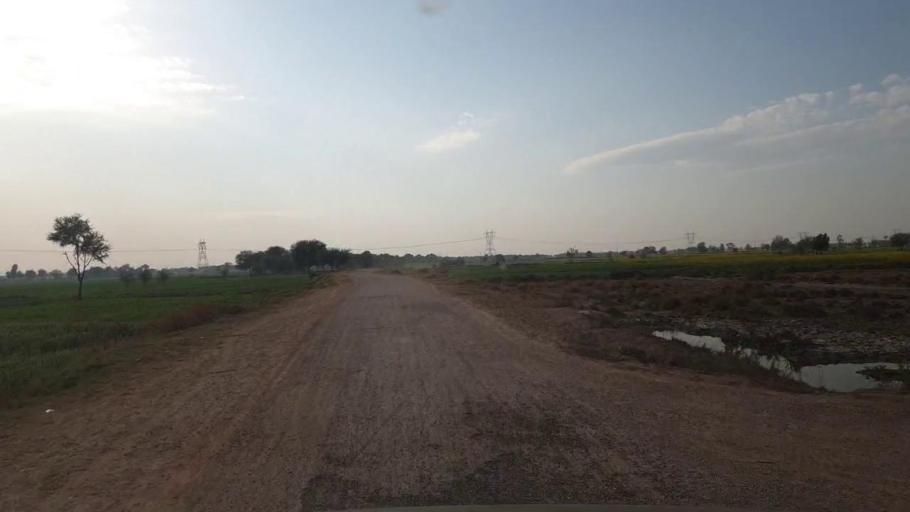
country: PK
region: Sindh
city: Sakrand
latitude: 26.0262
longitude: 68.3837
